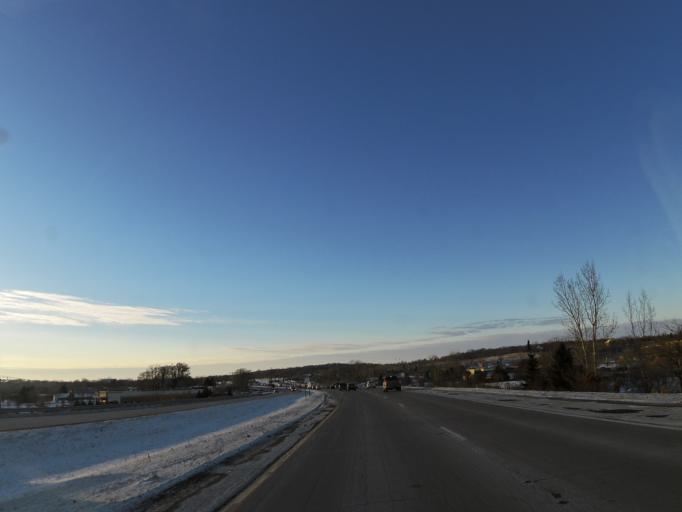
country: US
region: Minnesota
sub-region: Carver County
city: Chanhassen
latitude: 44.8604
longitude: -93.5440
